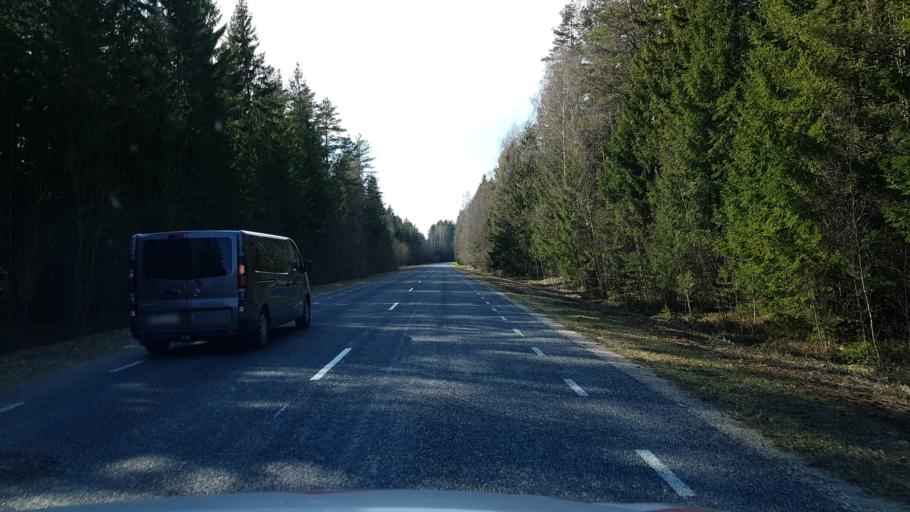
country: EE
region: Harju
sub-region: Loksa linn
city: Loksa
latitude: 59.5641
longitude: 25.9528
